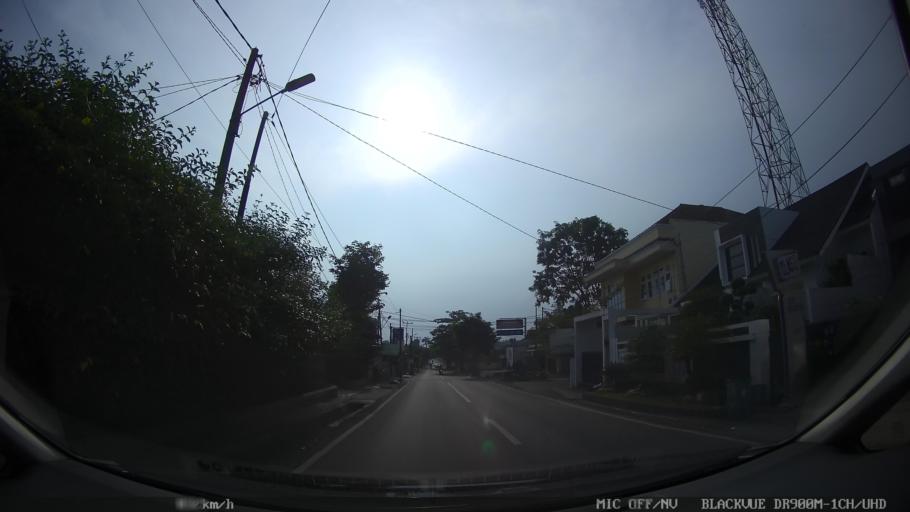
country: ID
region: Lampung
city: Bandarlampung
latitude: -5.4204
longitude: 105.2639
